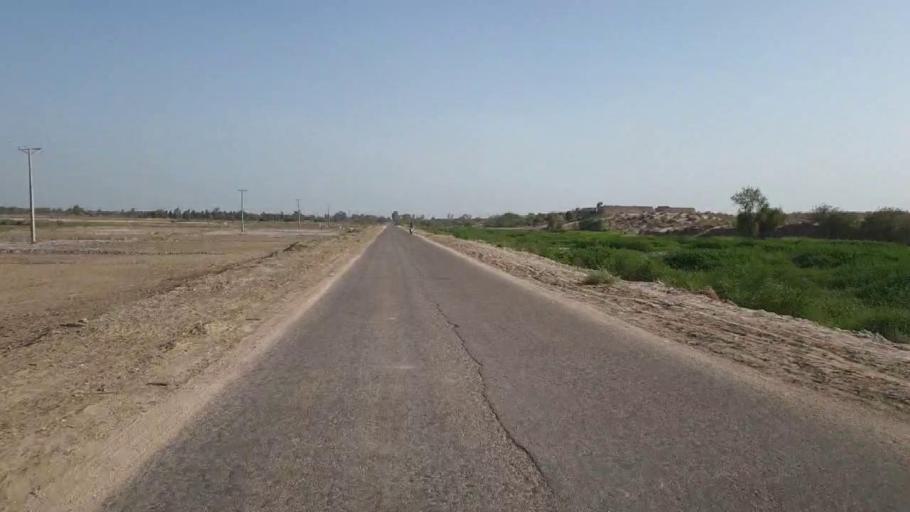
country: PK
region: Sindh
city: Daur
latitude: 26.4717
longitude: 68.4536
